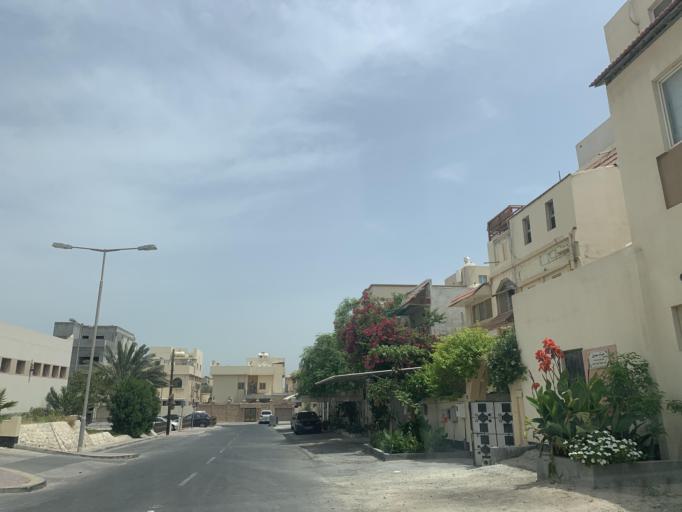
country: BH
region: Northern
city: Ar Rifa'
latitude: 26.1323
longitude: 50.5737
